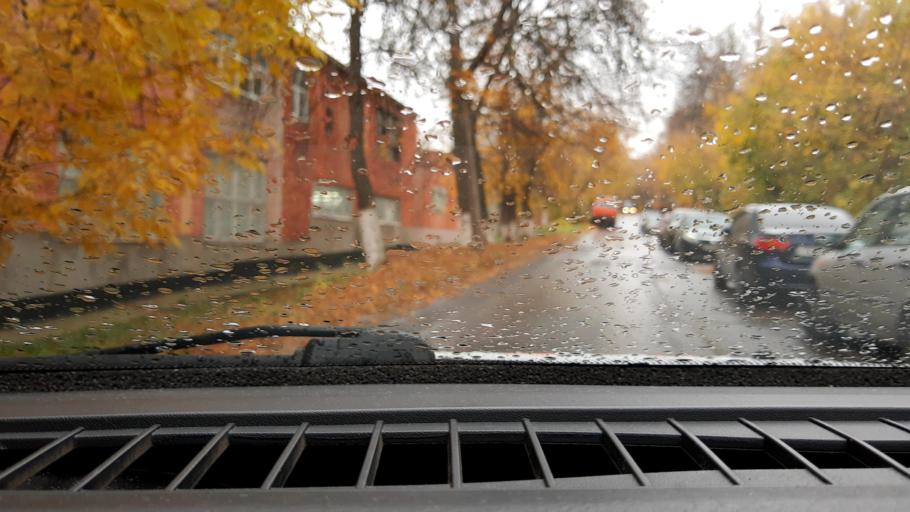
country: RU
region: Nizjnij Novgorod
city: Nizhniy Novgorod
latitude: 56.2461
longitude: 43.9775
